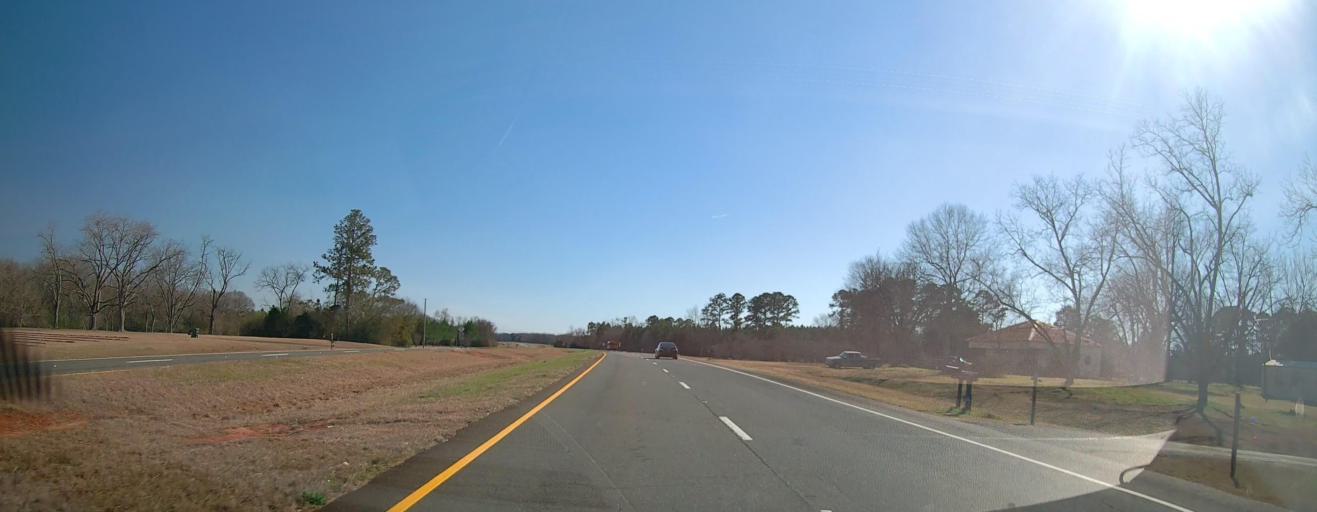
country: US
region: Georgia
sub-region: Schley County
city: Ellaville
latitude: 32.1574
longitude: -84.2705
